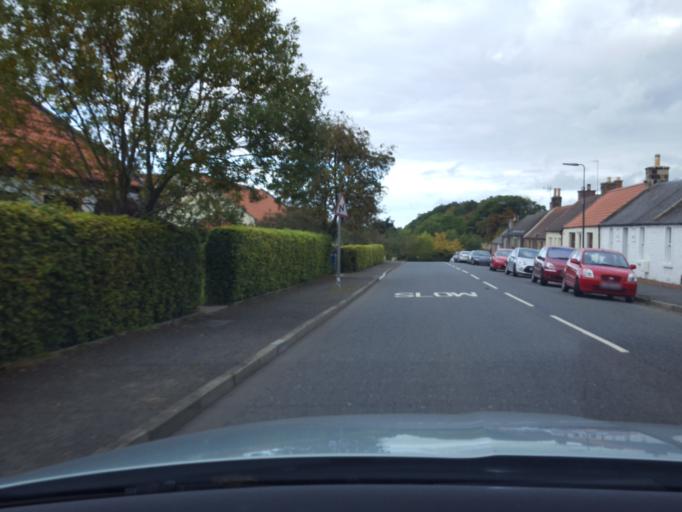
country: GB
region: Scotland
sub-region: Fife
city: Pathhead
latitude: 55.8667
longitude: -2.9942
